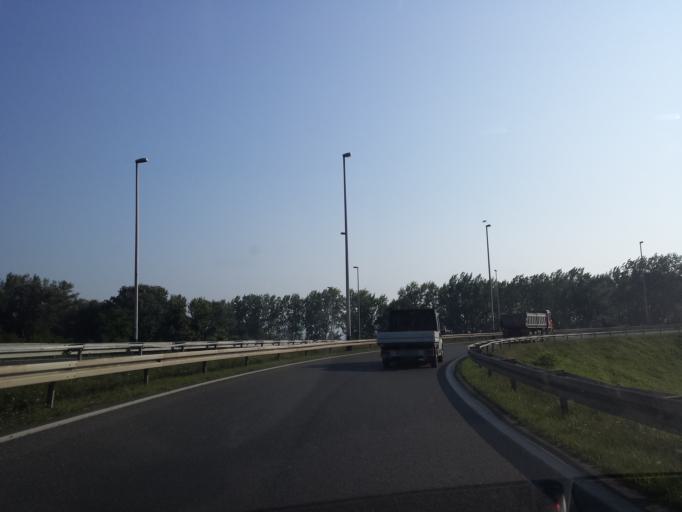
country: HR
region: Grad Zagreb
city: Jezdovec
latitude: 45.7898
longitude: 15.8464
